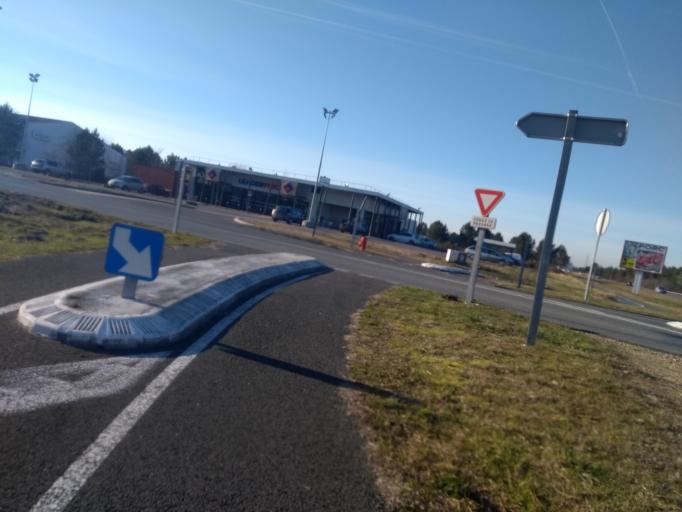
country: FR
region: Aquitaine
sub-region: Departement de la Gironde
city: Le Barp
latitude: 44.6207
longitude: -0.7841
